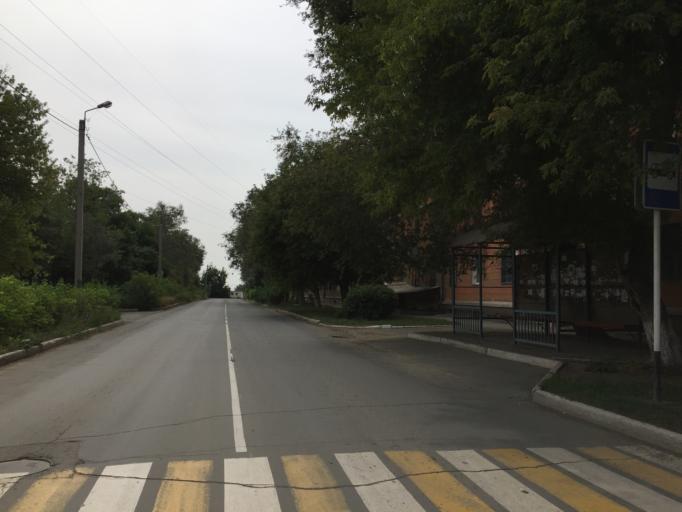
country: RU
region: Orenburg
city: Novotroitsk
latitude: 51.1954
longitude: 58.3143
